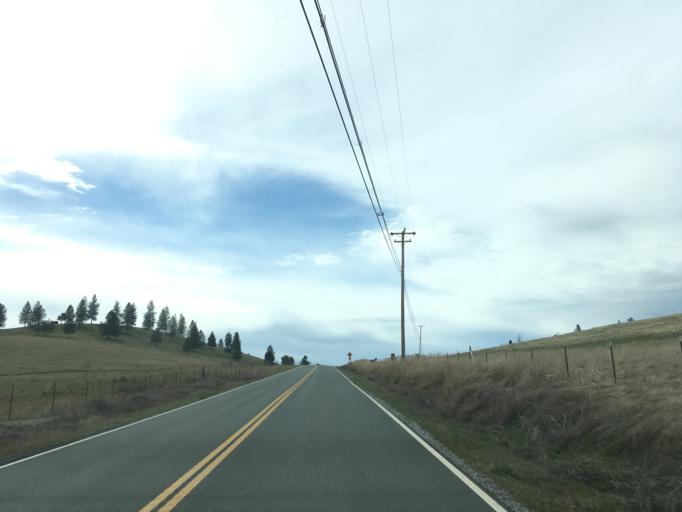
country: US
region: California
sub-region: Calaveras County
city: Mountain Ranch
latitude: 38.2175
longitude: -120.5527
